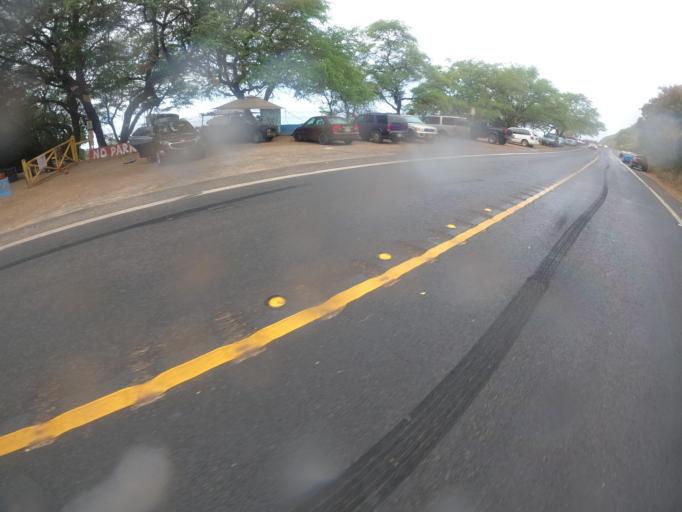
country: US
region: Hawaii
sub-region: Honolulu County
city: Makaha Valley
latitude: 21.5372
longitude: -158.2309
